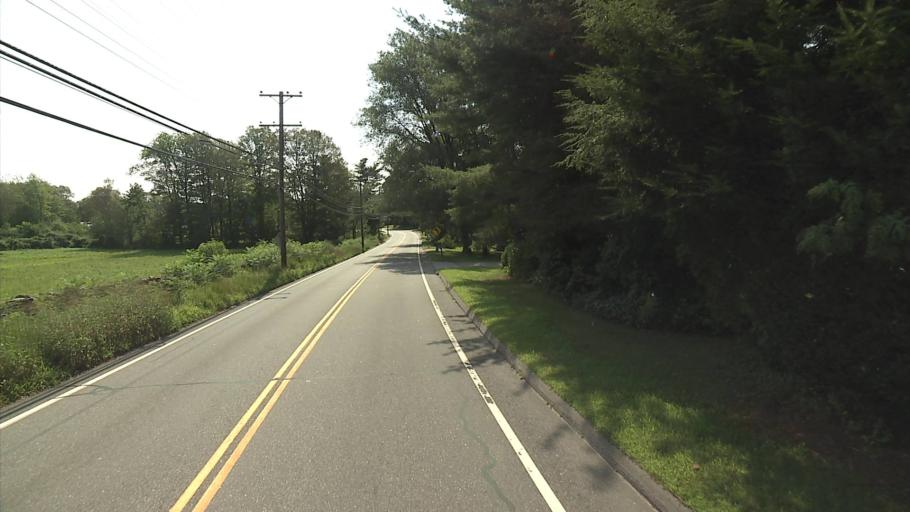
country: US
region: Connecticut
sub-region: New London County
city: Montville Center
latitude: 41.5645
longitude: -72.1610
